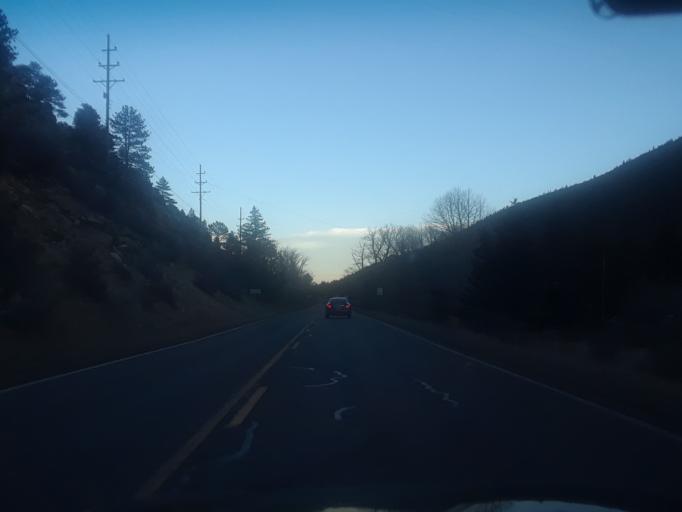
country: US
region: Colorado
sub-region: Clear Creek County
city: Georgetown
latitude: 39.4596
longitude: -105.6619
